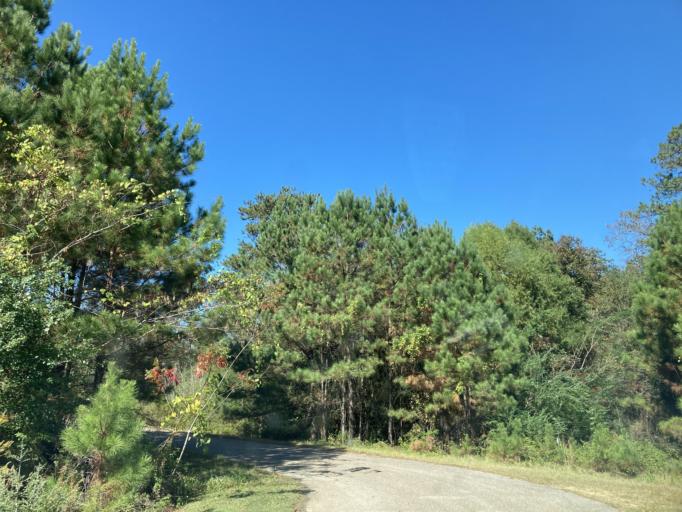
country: US
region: Mississippi
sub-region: Lamar County
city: Sumrall
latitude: 31.3083
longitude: -89.4951
